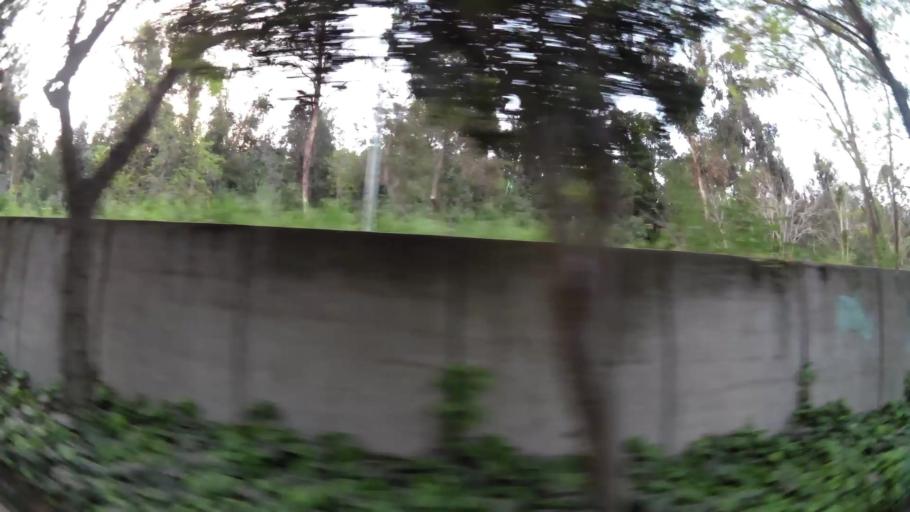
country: CL
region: Santiago Metropolitan
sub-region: Provincia de Santiago
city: Santiago
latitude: -33.4161
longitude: -70.6182
